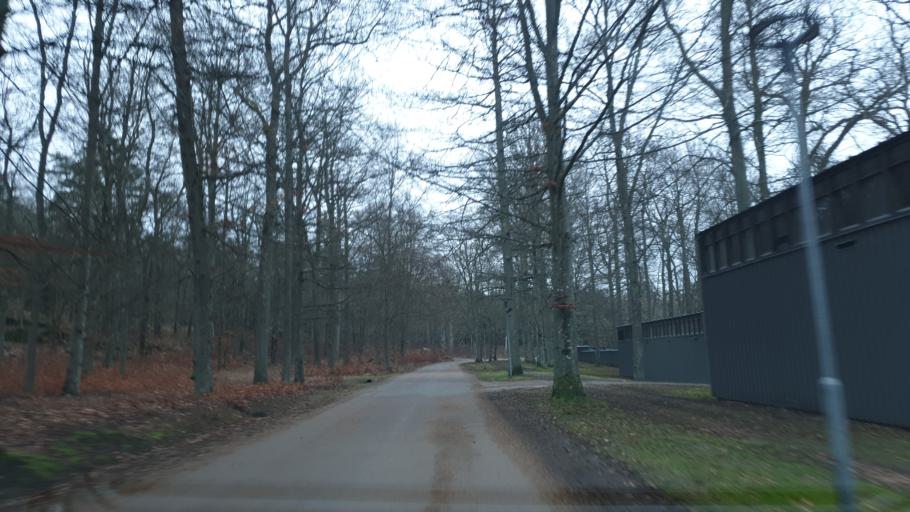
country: SE
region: Blekinge
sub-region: Karlskrona Kommun
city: Rodeby
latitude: 56.2153
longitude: 15.6833
